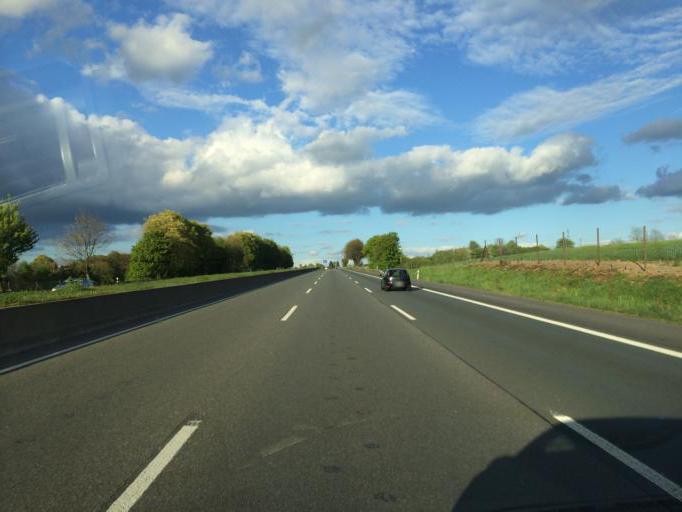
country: DE
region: North Rhine-Westphalia
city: Burscheid
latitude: 51.0743
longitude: 7.1134
